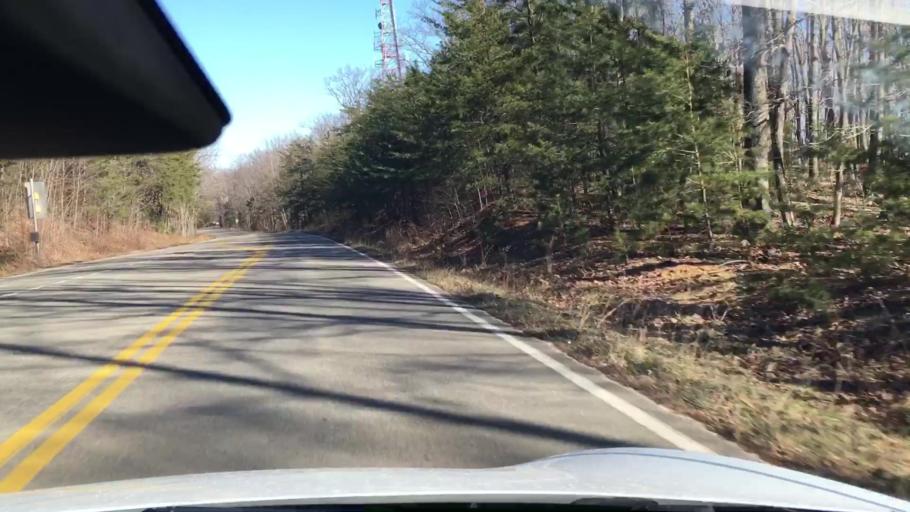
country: US
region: Virginia
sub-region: Powhatan County
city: Powhatan
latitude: 37.5248
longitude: -77.8029
